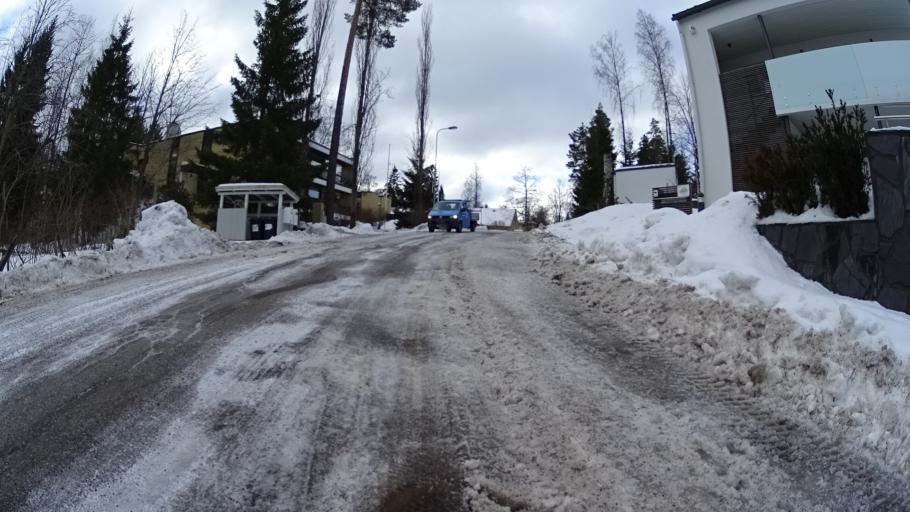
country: FI
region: Uusimaa
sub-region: Helsinki
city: Kauniainen
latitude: 60.2198
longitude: 24.7367
